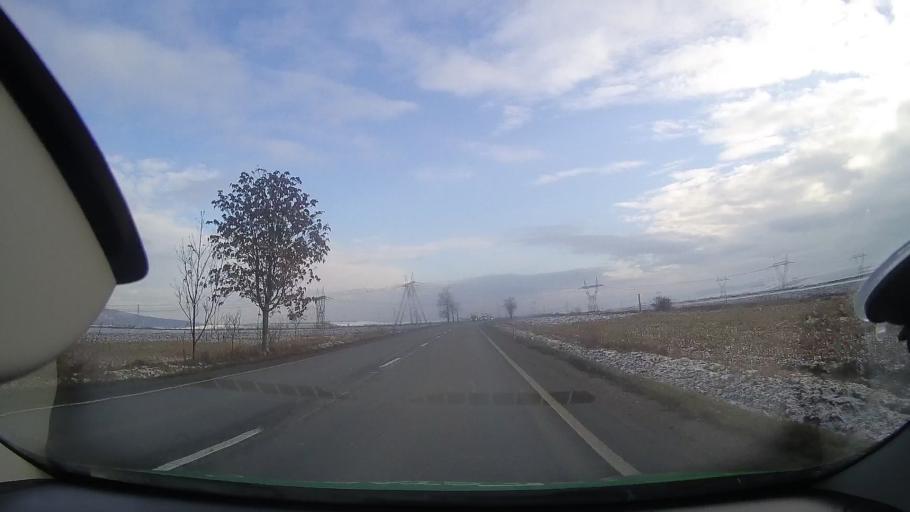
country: RO
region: Mures
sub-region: Comuna Cuci
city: Cuci
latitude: 46.4546
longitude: 24.1817
